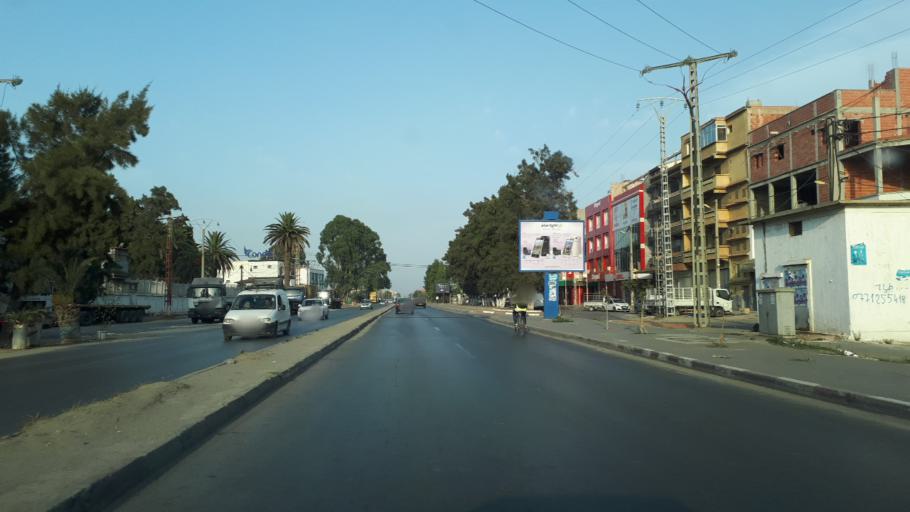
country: DZ
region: Alger
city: Dar el Beida
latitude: 36.7286
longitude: 3.2210
